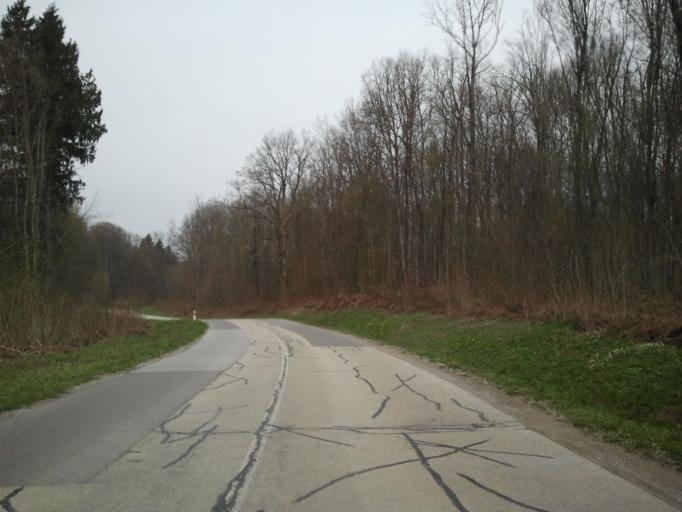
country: HR
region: Sisacko-Moslavacka
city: Gvozd
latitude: 45.3113
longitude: 15.9685
